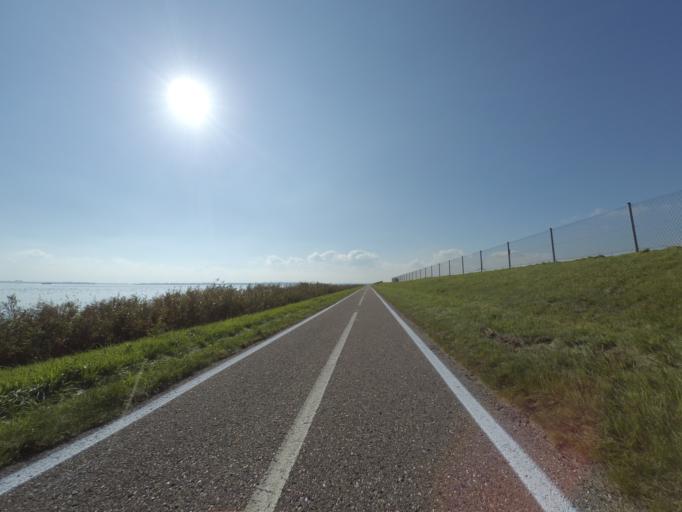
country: NL
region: Flevoland
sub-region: Gemeente Zeewolde
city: Zeewolde
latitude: 52.3608
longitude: 5.5534
